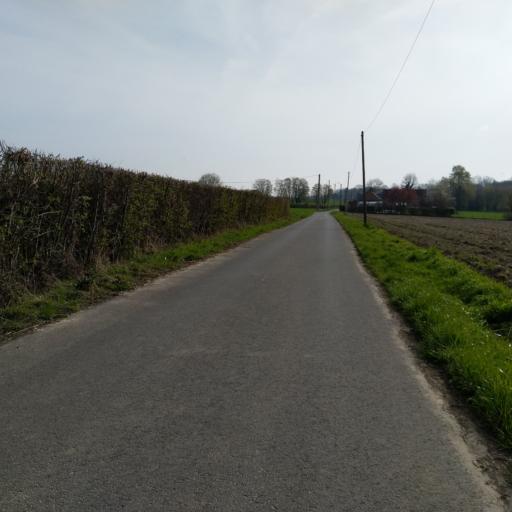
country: FR
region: Nord-Pas-de-Calais
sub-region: Departement du Nord
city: Feignies
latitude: 50.3287
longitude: 3.8816
